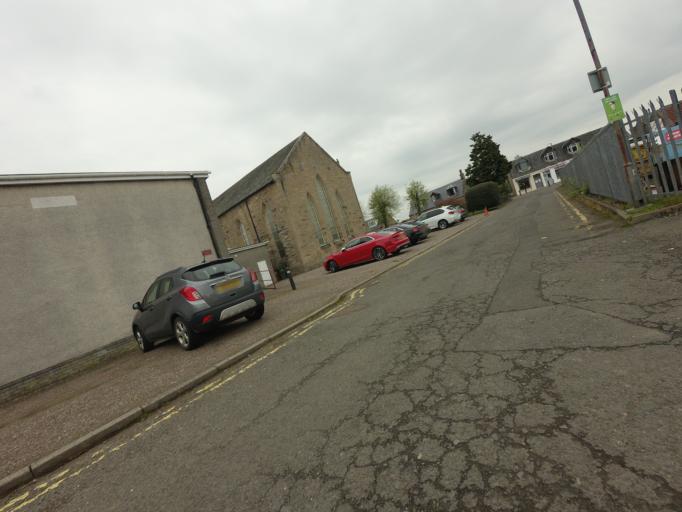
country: GB
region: Scotland
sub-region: Falkirk
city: Polmont
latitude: 55.9813
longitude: -3.7185
